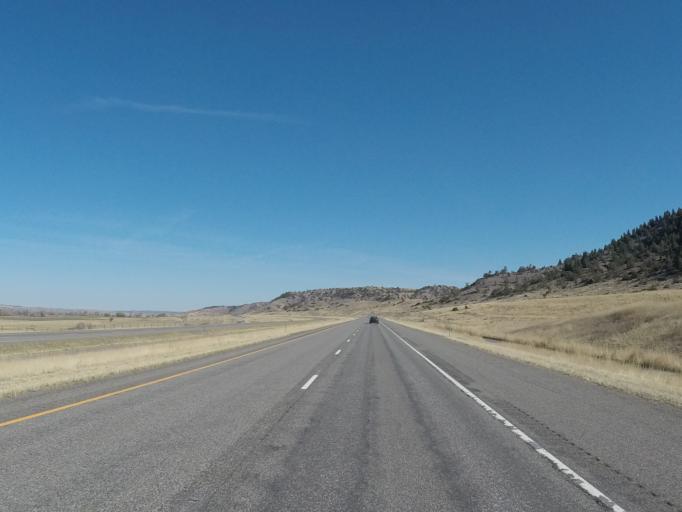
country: US
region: Montana
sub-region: Sweet Grass County
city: Big Timber
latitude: 45.7639
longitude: -110.0981
